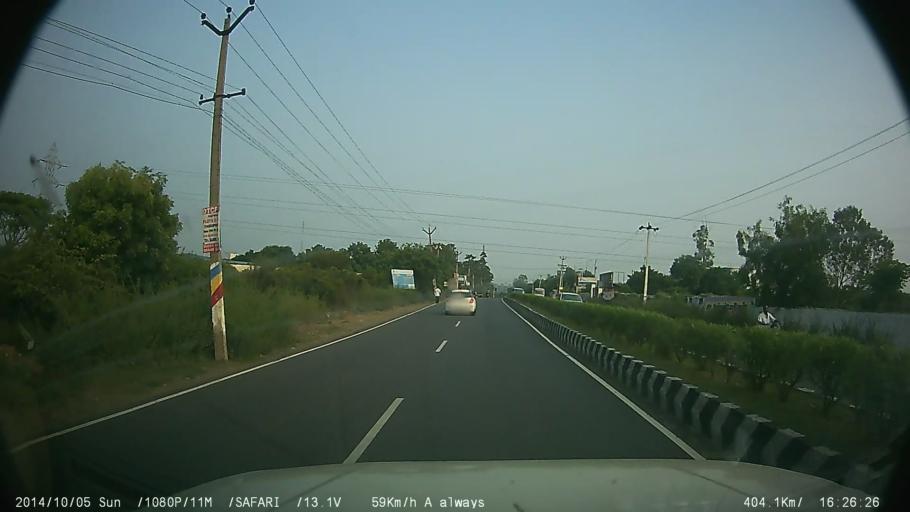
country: IN
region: Tamil Nadu
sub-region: Kancheepuram
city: Vengavasal
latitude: 12.8069
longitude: 80.1885
